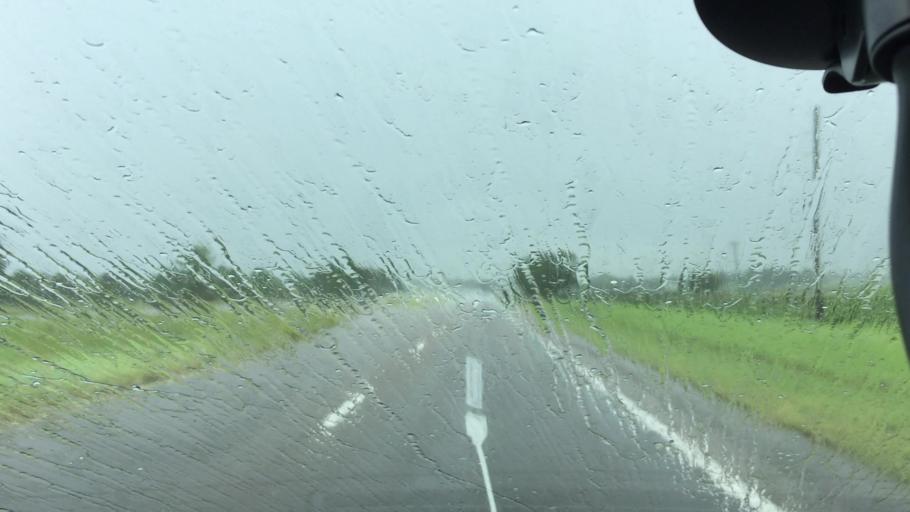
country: US
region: Alabama
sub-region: Montgomery County
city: Pike Road
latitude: 32.2335
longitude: -86.1243
